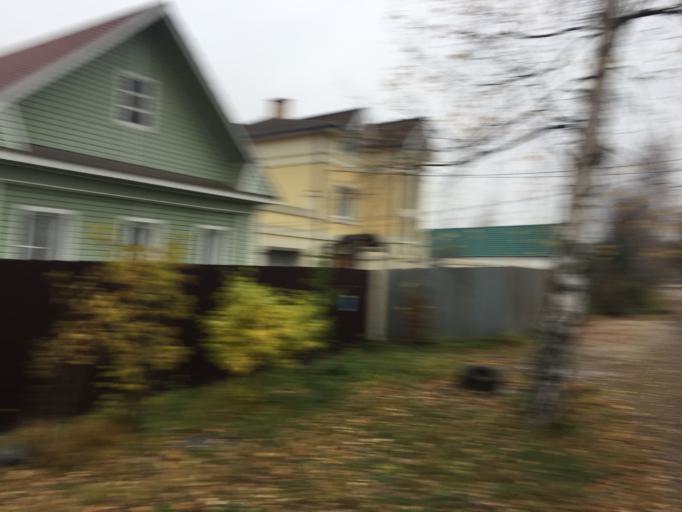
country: RU
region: Jaroslavl
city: Yaroslavl
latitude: 57.7232
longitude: 39.7697
